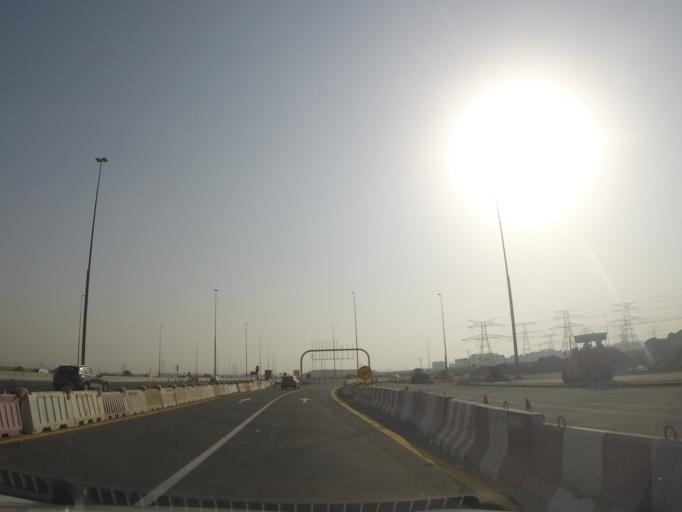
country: AE
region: Dubai
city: Dubai
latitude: 25.0332
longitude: 55.1658
